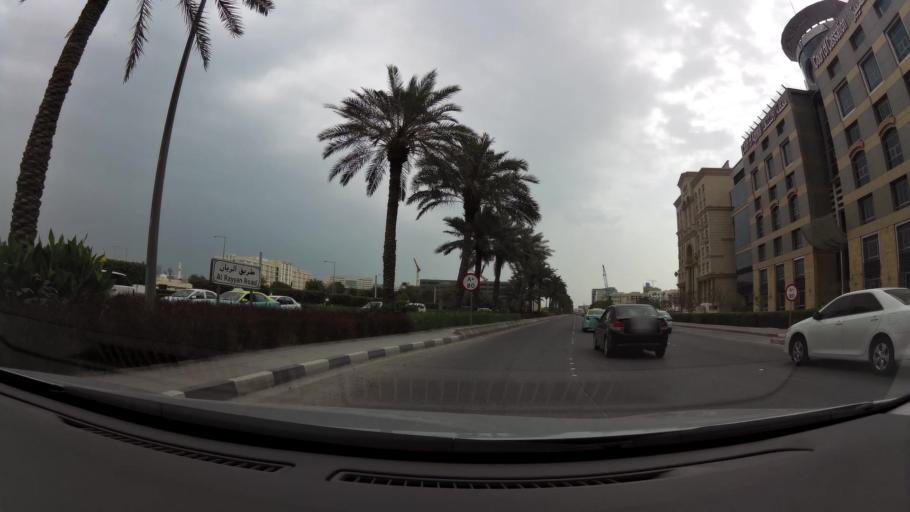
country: QA
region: Baladiyat ad Dawhah
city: Doha
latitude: 25.2921
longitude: 51.4972
